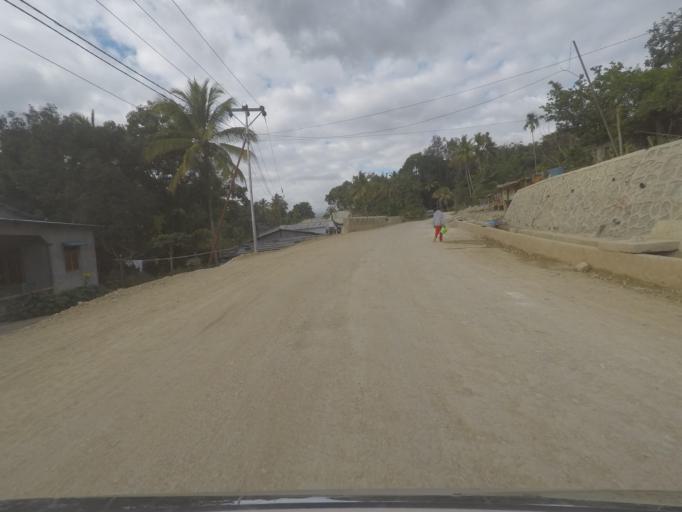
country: TL
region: Baucau
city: Venilale
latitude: -8.5967
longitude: 126.3858
